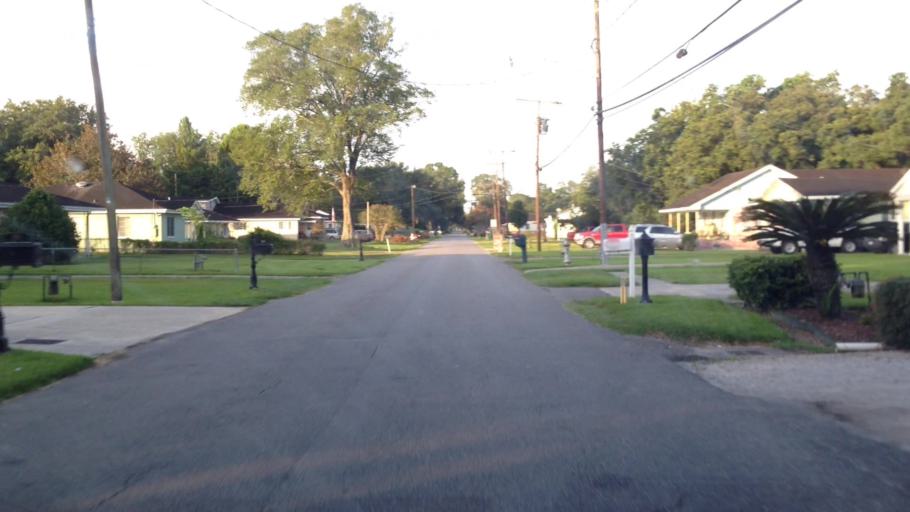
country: US
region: Louisiana
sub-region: Jefferson Parish
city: Bridge City
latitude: 29.9381
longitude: -90.1562
